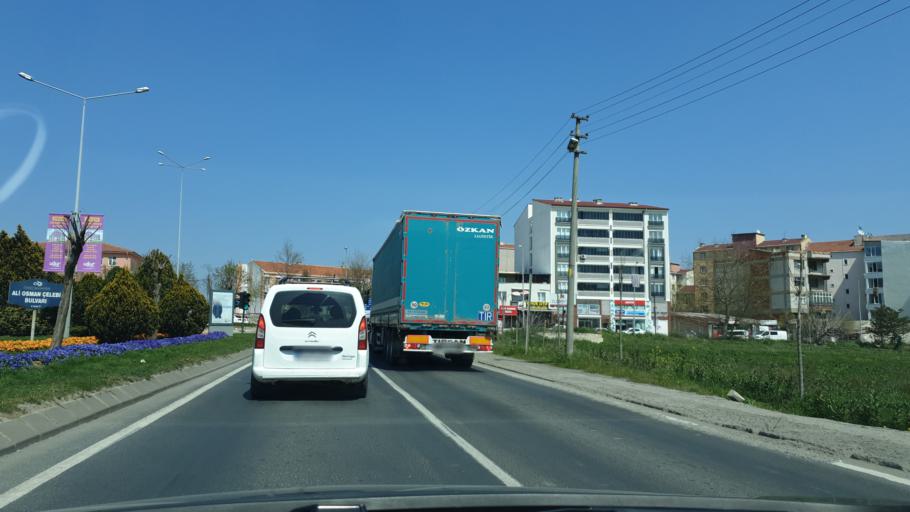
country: TR
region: Tekirdag
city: Corlu
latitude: 41.1629
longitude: 27.7876
